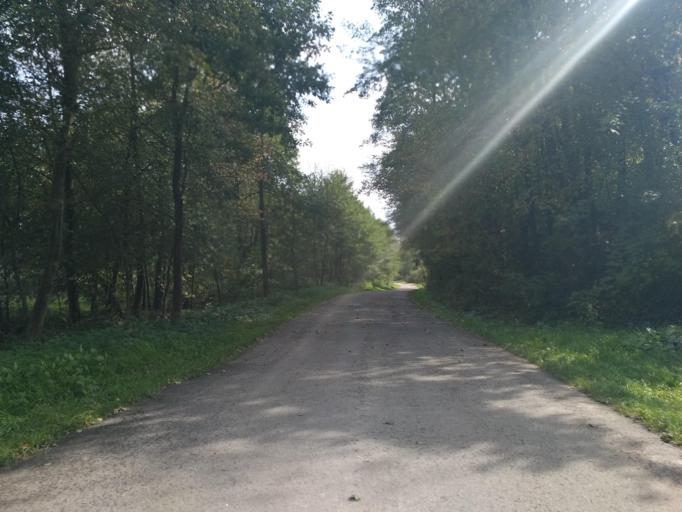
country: PL
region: Subcarpathian Voivodeship
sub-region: Powiat ropczycko-sedziszowski
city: Niedzwiada
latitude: 49.9369
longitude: 21.5307
